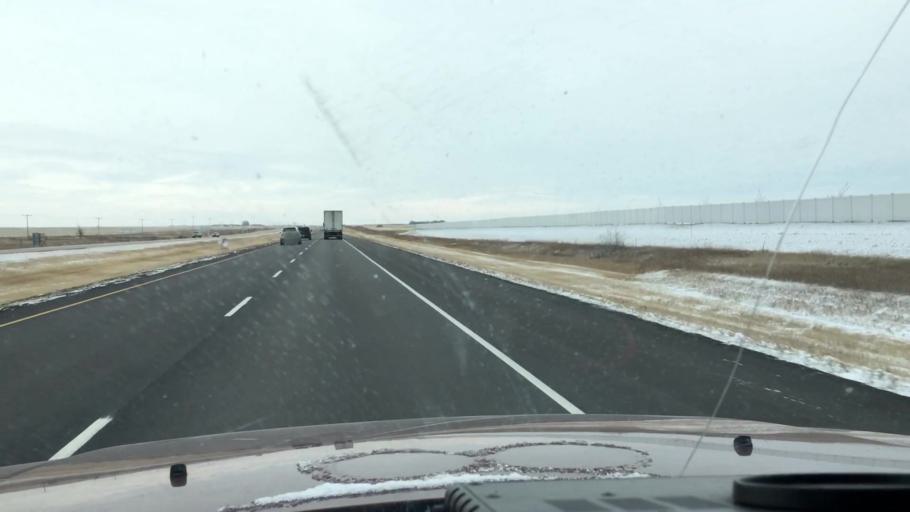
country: CA
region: Saskatchewan
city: Saskatoon
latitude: 51.8055
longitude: -106.4929
